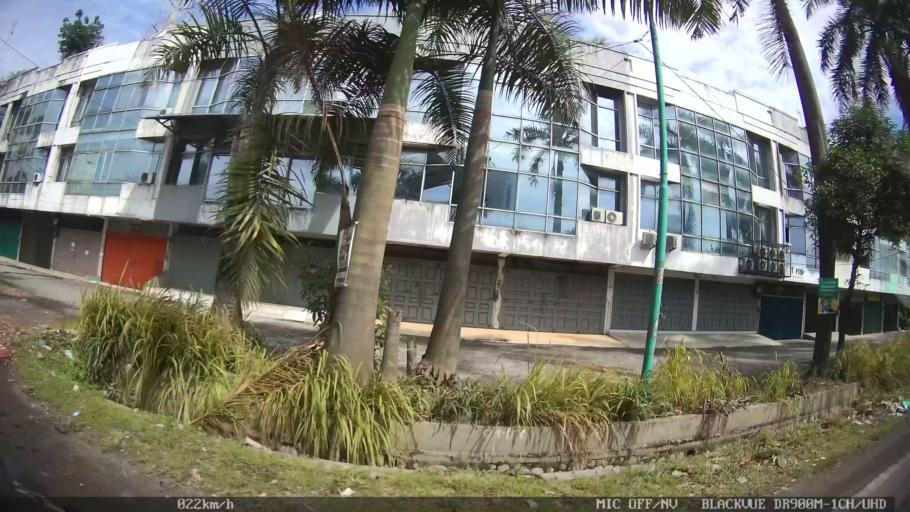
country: ID
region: North Sumatra
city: Medan
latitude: 3.6211
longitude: 98.6577
